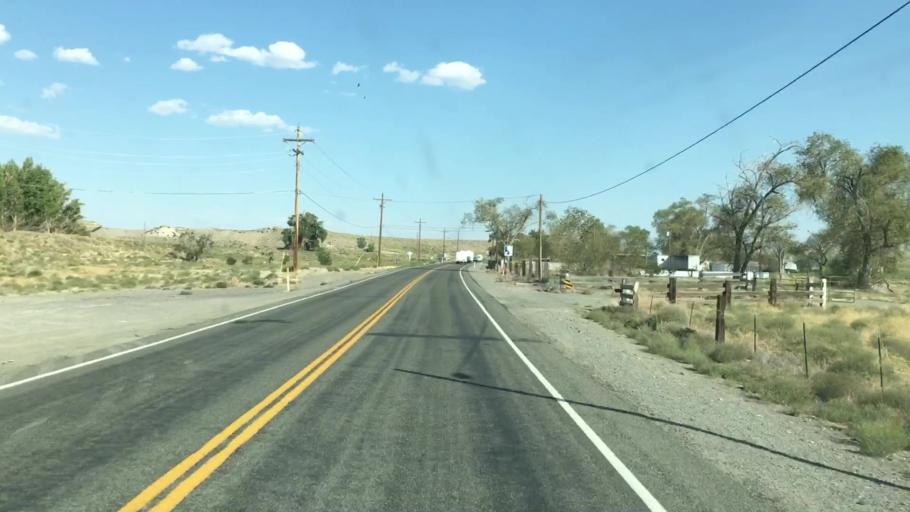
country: US
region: Nevada
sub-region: Lyon County
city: Fernley
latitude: 39.6315
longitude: -119.2815
